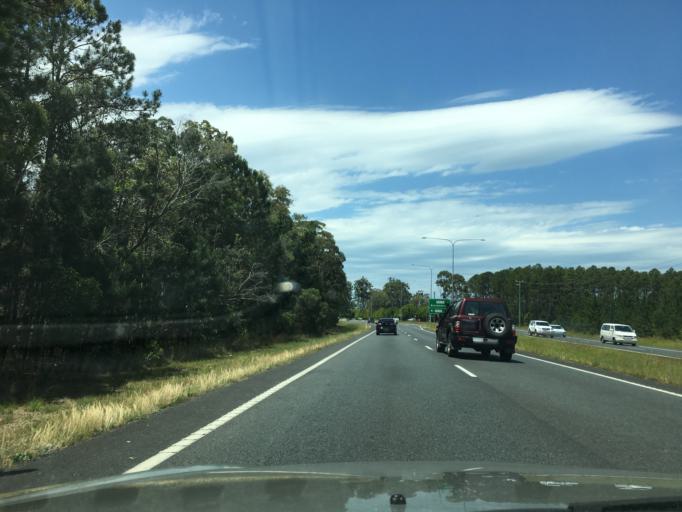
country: AU
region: Queensland
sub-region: Moreton Bay
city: Caboolture
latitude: -27.0757
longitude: 153.0495
